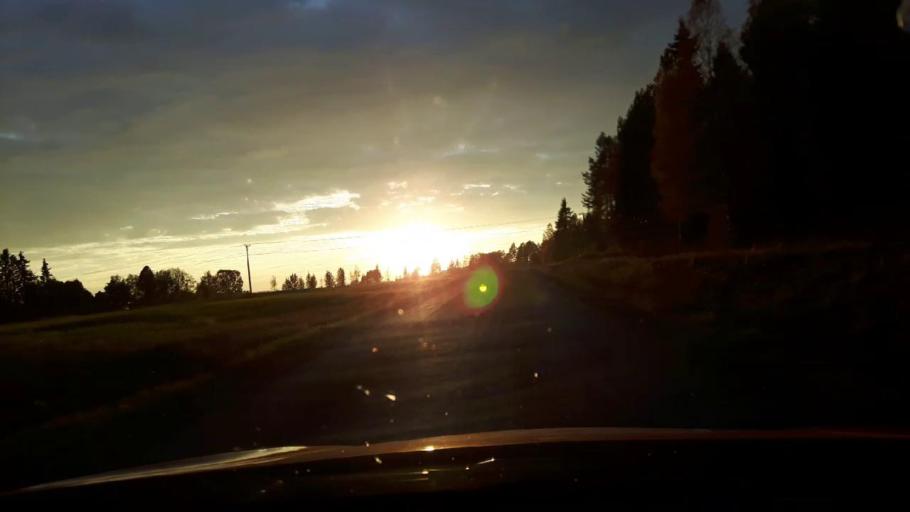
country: SE
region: Jaemtland
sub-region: OEstersunds Kommun
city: Lit
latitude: 63.2897
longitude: 14.8419
